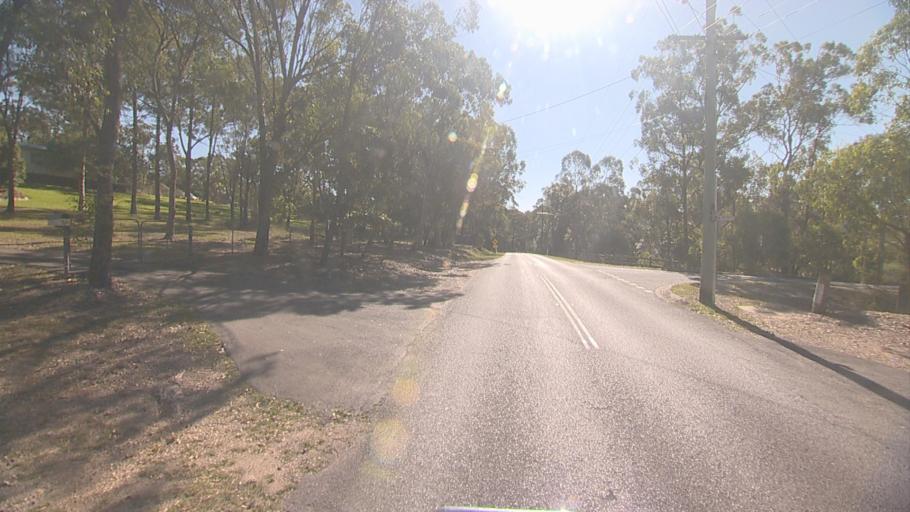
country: AU
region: Queensland
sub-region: Logan
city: Springwood
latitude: -27.5990
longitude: 153.1651
